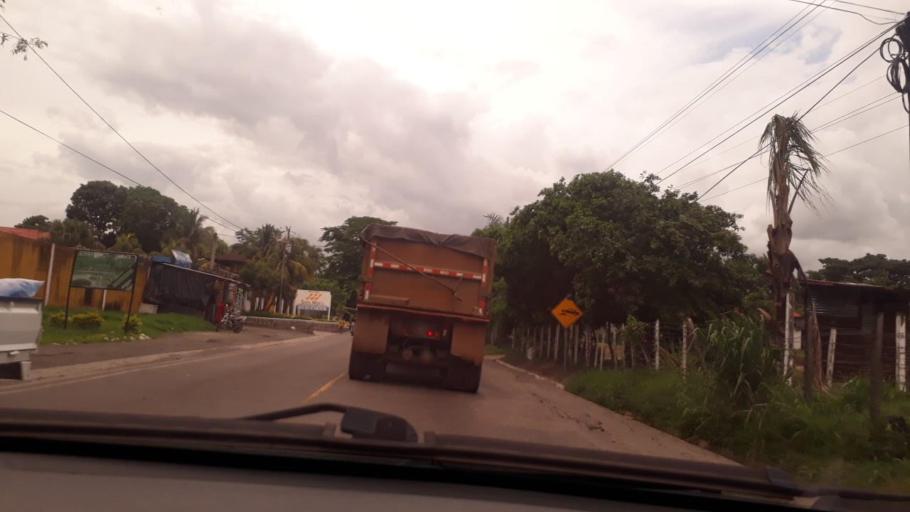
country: GT
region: Izabal
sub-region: Municipio de Los Amates
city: Los Amates
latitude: 15.2542
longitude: -89.1006
